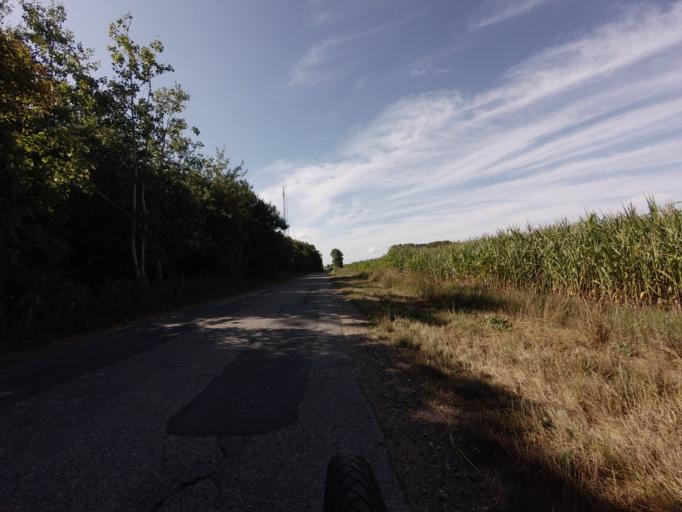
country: DK
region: North Denmark
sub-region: Hjorring Kommune
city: Vra
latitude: 57.4062
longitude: 9.9561
